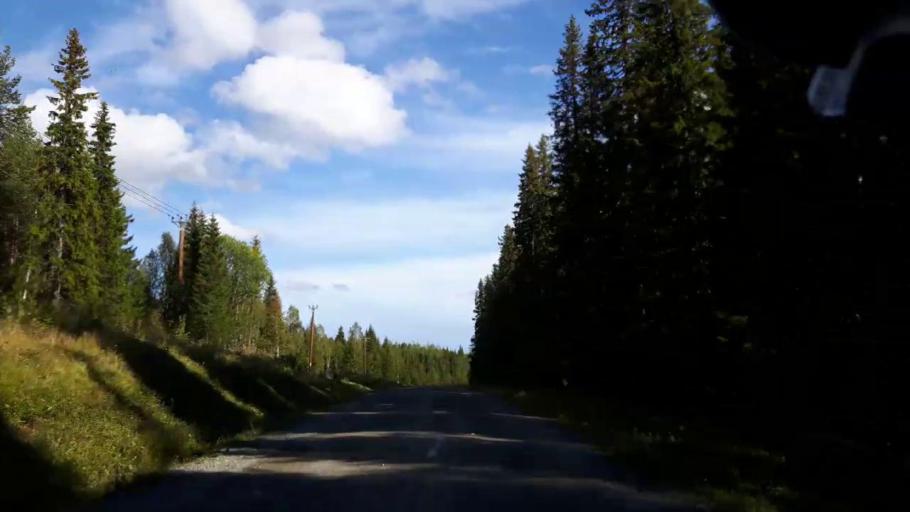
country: SE
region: Jaemtland
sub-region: Ragunda Kommun
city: Hammarstrand
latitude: 63.4338
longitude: 16.0354
